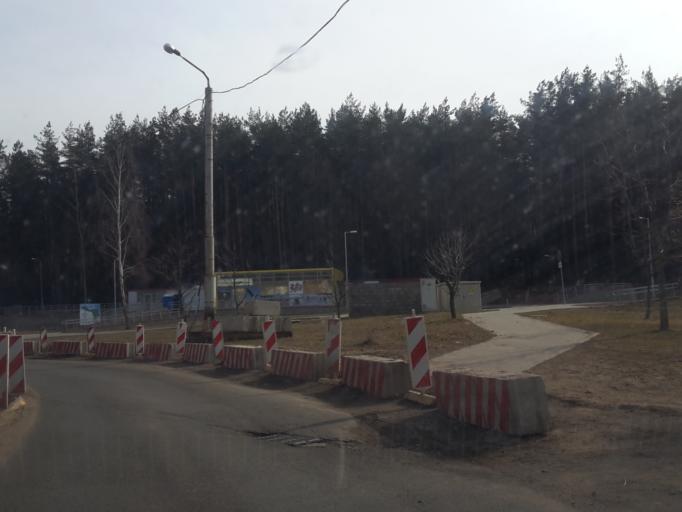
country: BY
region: Minsk
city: Vyaliki Trastsyanets
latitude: 53.9016
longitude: 27.6629
